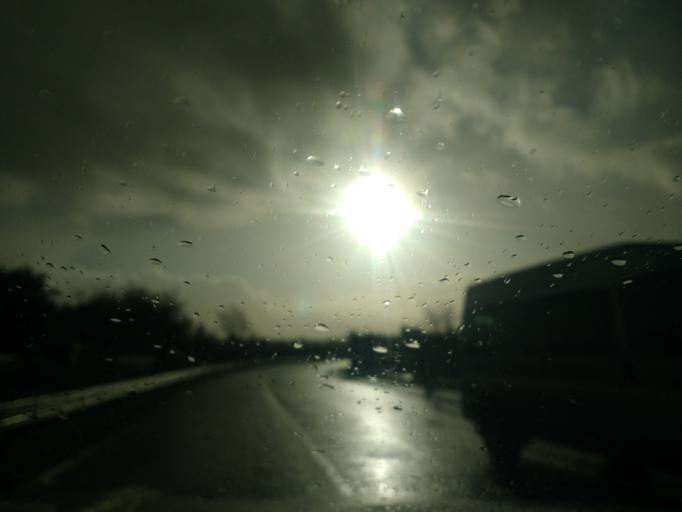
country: IE
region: Ulster
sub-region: County Donegal
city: Letterkenny
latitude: 54.9635
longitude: -7.6916
